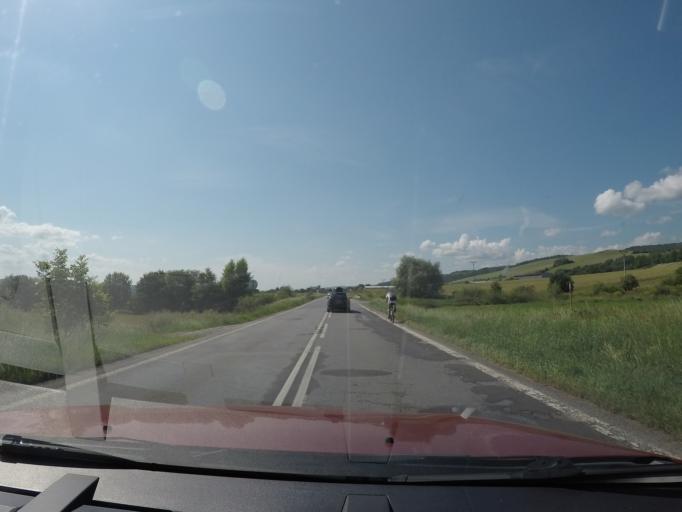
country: SK
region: Presovsky
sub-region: Okres Presov
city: Presov
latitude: 48.9373
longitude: 21.2402
